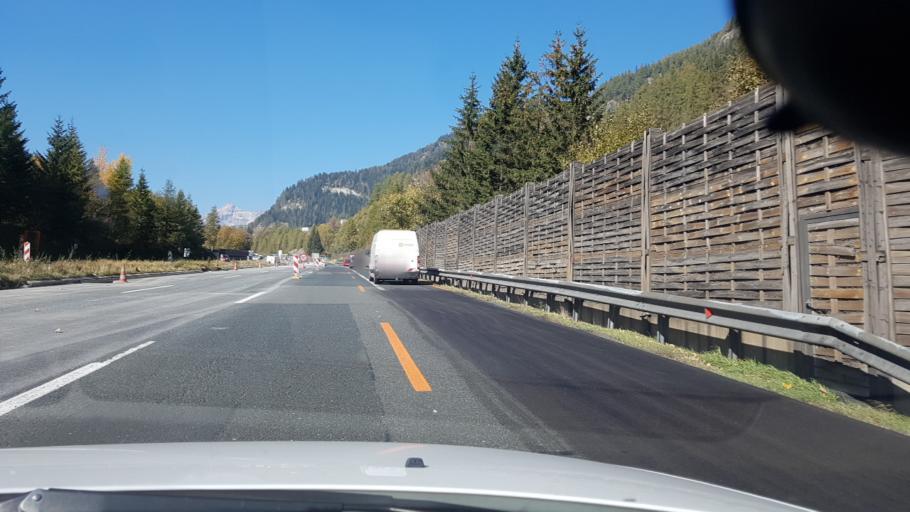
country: AT
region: Salzburg
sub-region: Politischer Bezirk Tamsweg
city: Zederhaus
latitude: 47.1332
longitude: 13.5468
